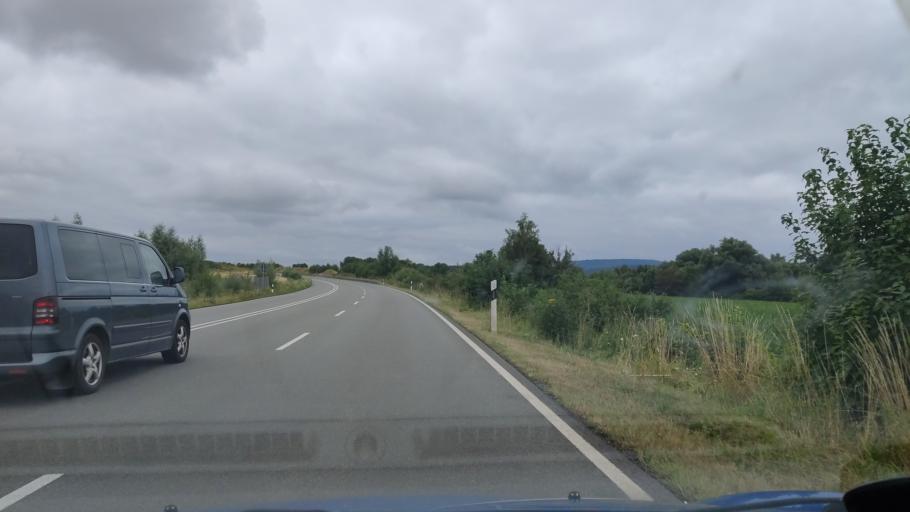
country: DE
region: Lower Saxony
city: Messenkamp
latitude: 52.2377
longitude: 9.3990
